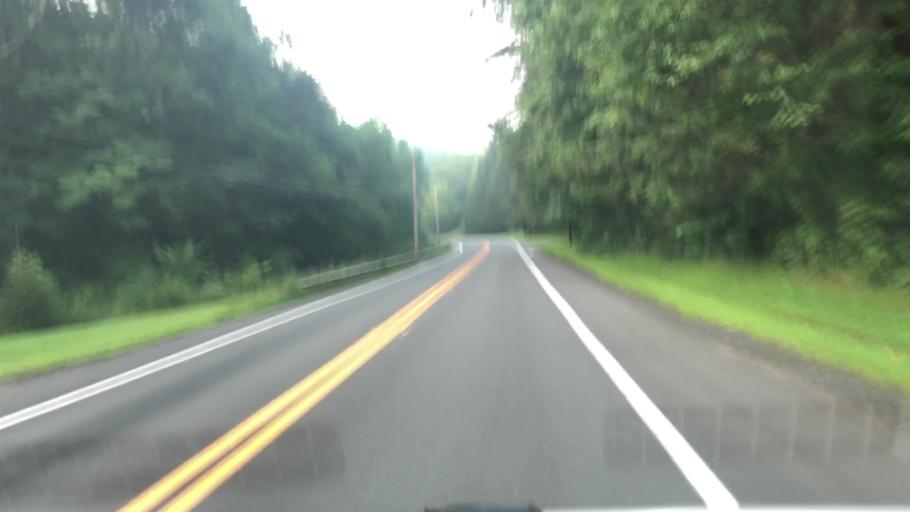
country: US
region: Massachusetts
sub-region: Franklin County
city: Buckland
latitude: 42.5623
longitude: -72.8042
